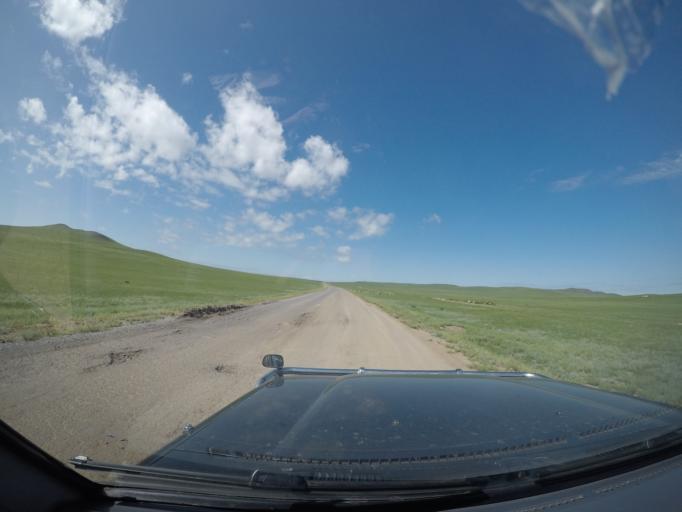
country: MN
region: Suhbaatar
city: Hanhohiy
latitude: 47.3846
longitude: 111.8585
